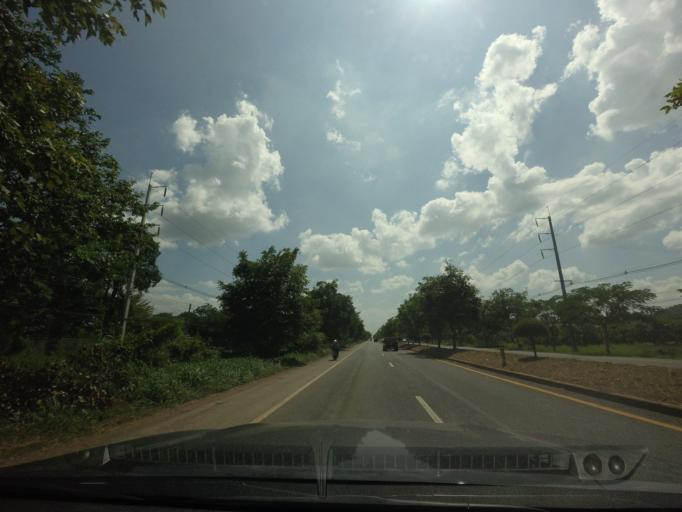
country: TH
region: Phetchabun
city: Nong Phai
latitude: 16.0258
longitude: 101.0749
